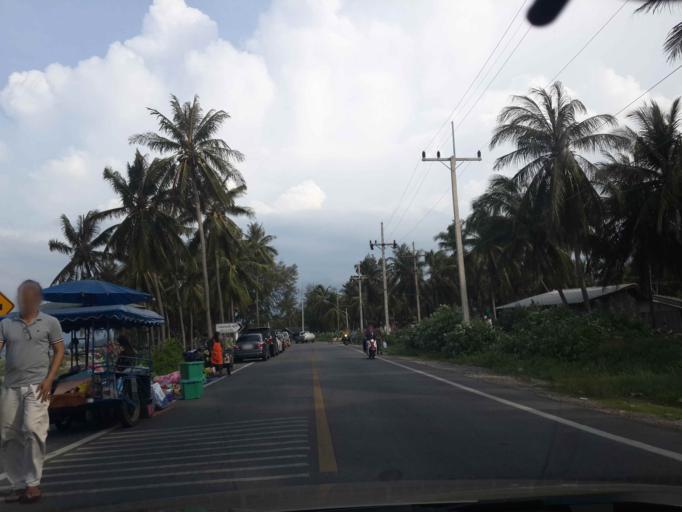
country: TH
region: Pattani
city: Yaring
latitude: 6.9154
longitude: 101.3388
